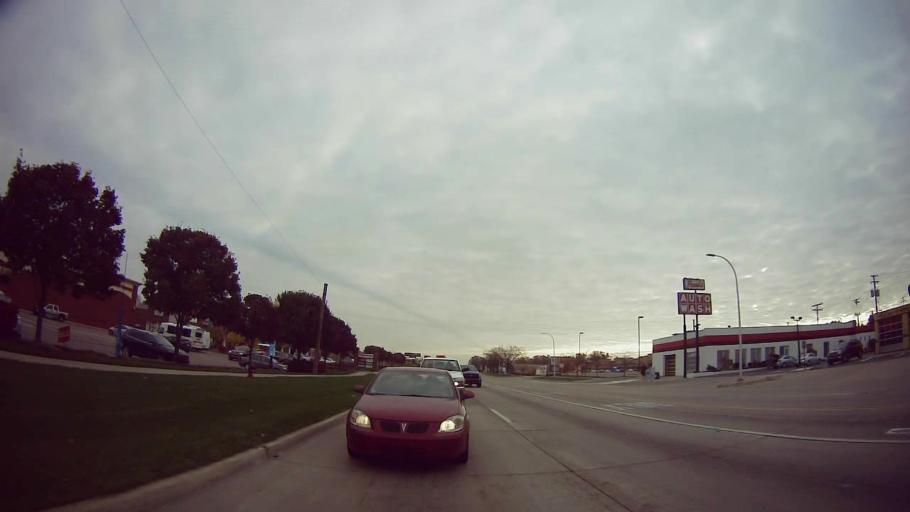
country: US
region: Michigan
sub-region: Oakland County
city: Clawson
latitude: 42.5331
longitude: -83.1655
